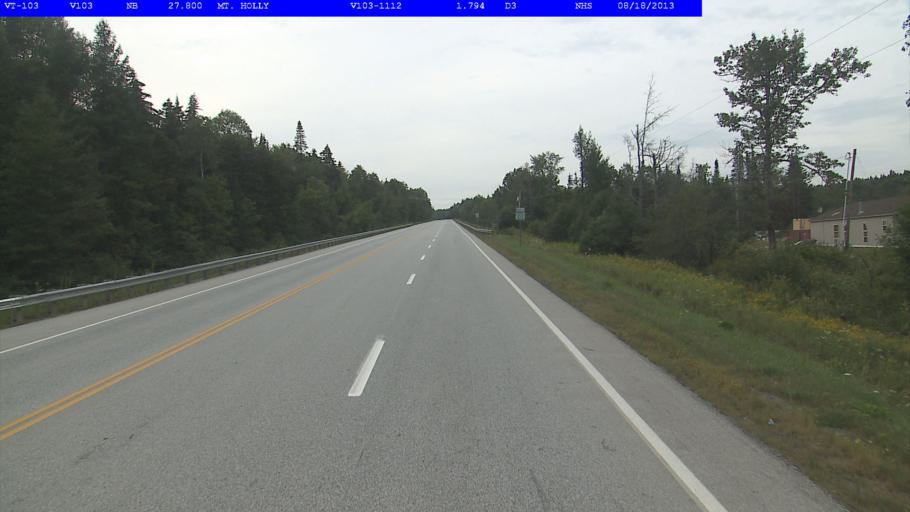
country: US
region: Vermont
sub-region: Windsor County
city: Chester
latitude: 43.4417
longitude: -72.7662
